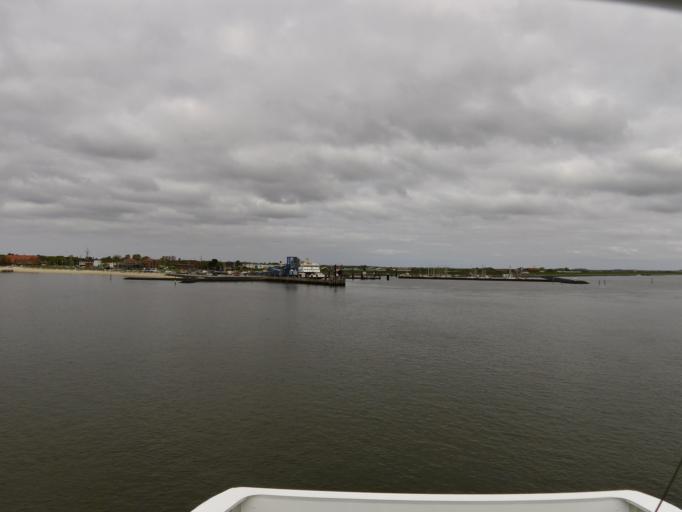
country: DE
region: Schleswig-Holstein
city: Wyk auf Fohr
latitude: 54.6911
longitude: 8.5818
